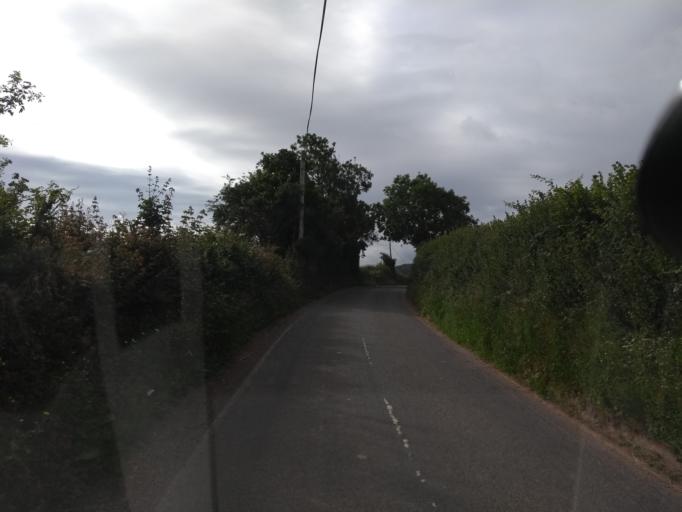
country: GB
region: England
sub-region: Somerset
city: Wiveliscombe
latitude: 51.0703
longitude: -3.2874
